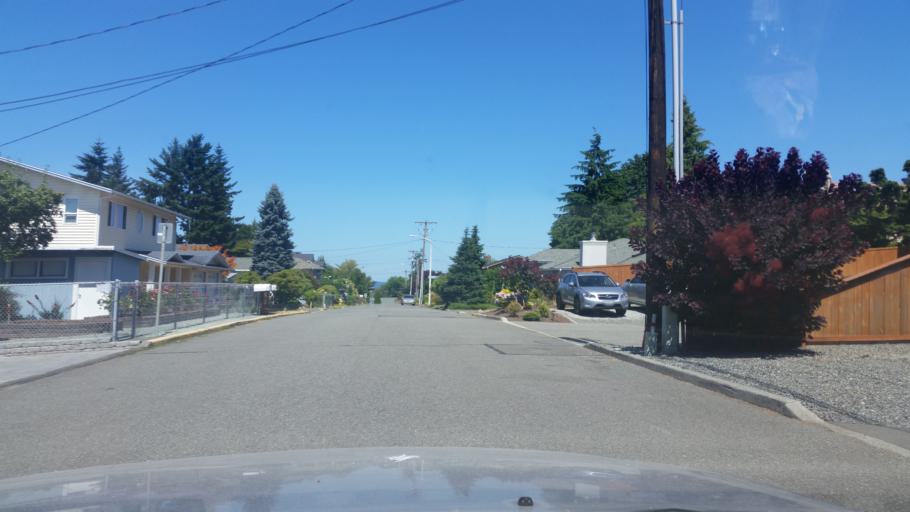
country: US
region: Washington
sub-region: Snohomish County
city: Edmonds
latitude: 47.8054
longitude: -122.3742
